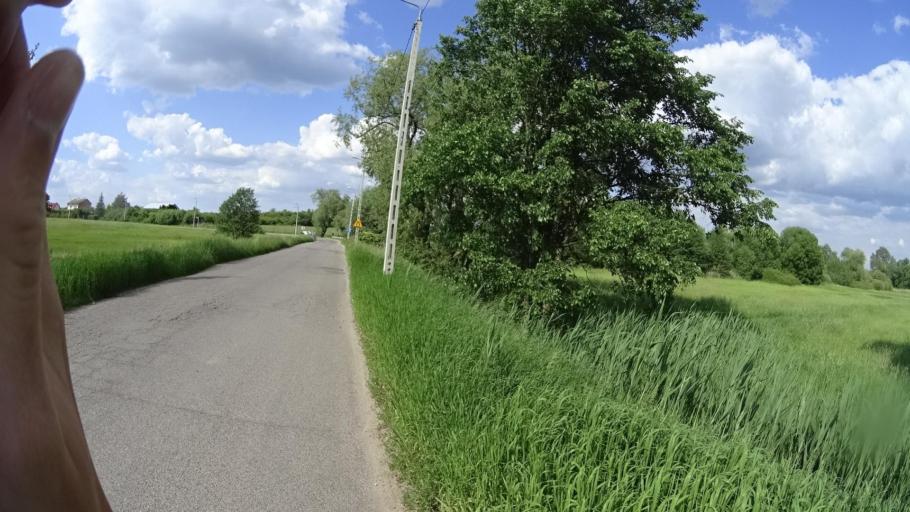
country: PL
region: Masovian Voivodeship
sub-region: Powiat piaseczynski
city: Tarczyn
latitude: 52.0343
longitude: 20.8239
